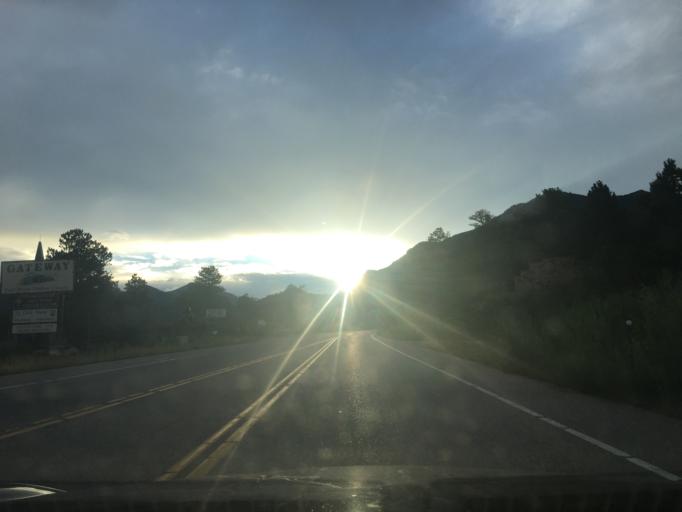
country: US
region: Colorado
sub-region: Larimer County
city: Estes Park
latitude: 40.4024
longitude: -105.5863
